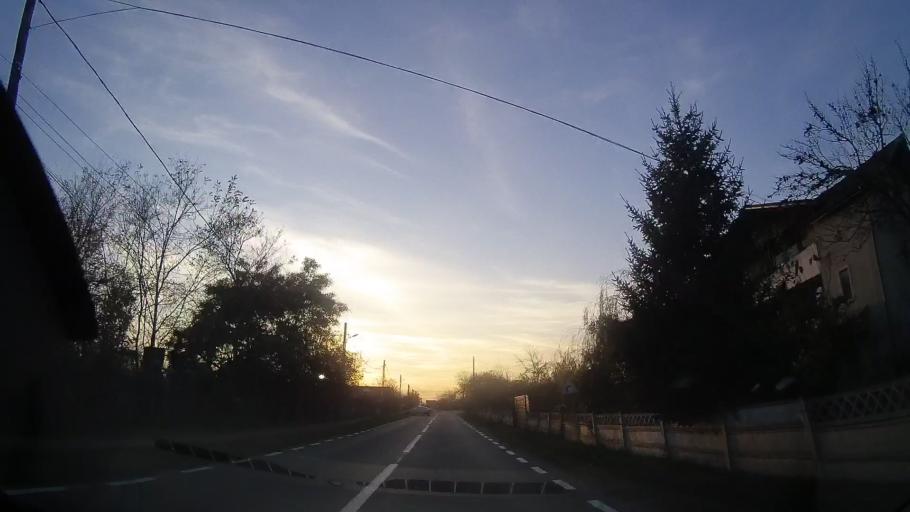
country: RO
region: Constanta
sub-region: Comuna Topraisar
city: Topraisar
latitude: 44.0109
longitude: 28.4469
